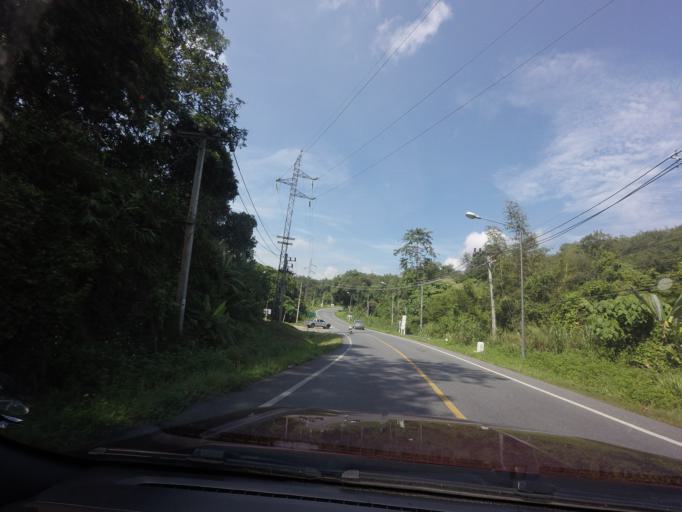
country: TH
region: Yala
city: Betong
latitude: 5.8656
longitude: 101.1279
